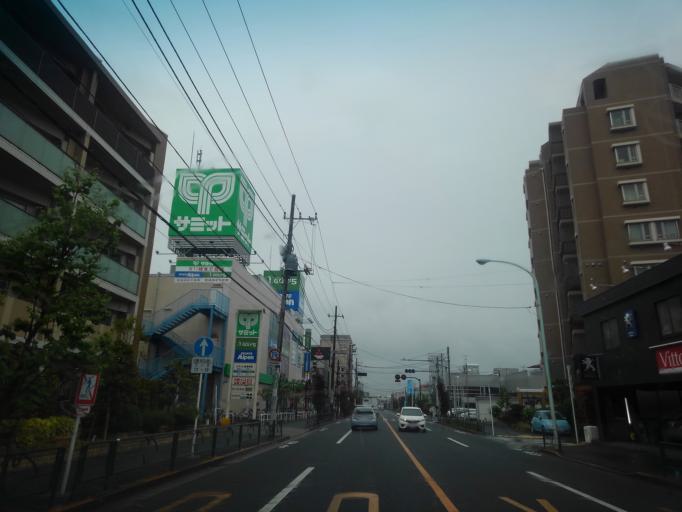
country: JP
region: Tokyo
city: Mitaka-shi
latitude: 35.6866
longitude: 139.6221
